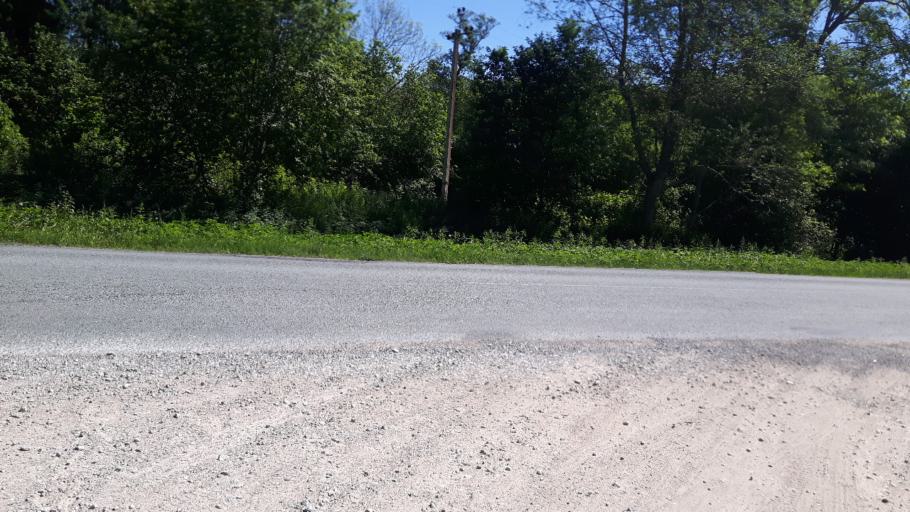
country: EE
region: Harju
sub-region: Kuusalu vald
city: Kuusalu
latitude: 59.5139
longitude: 25.5190
